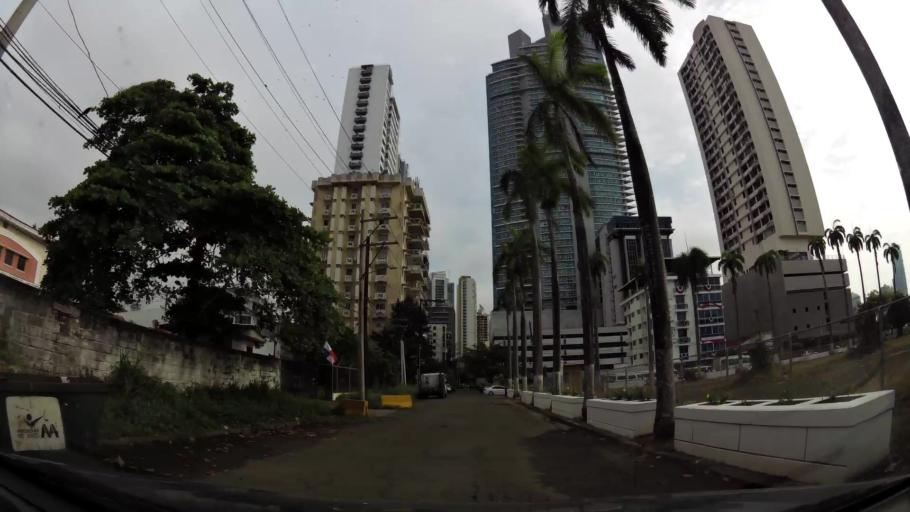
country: PA
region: Panama
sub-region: Distrito de Panama
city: Ancon
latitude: 8.9704
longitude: -79.5314
